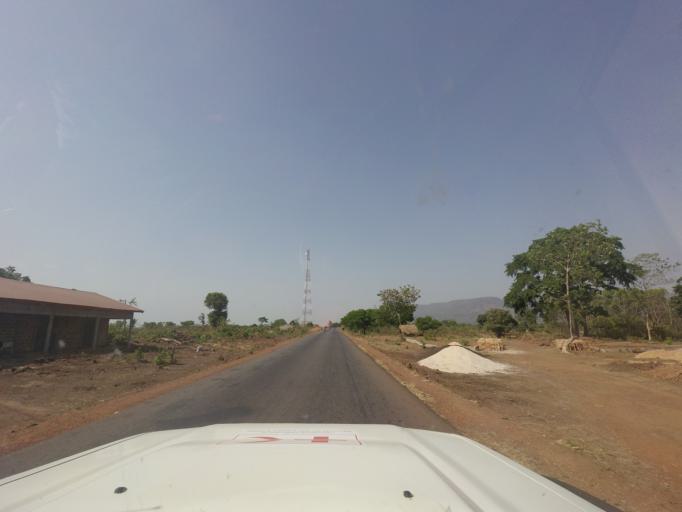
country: GN
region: Mamou
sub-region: Mamou Prefecture
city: Mamou
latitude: 10.2603
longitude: -12.4555
